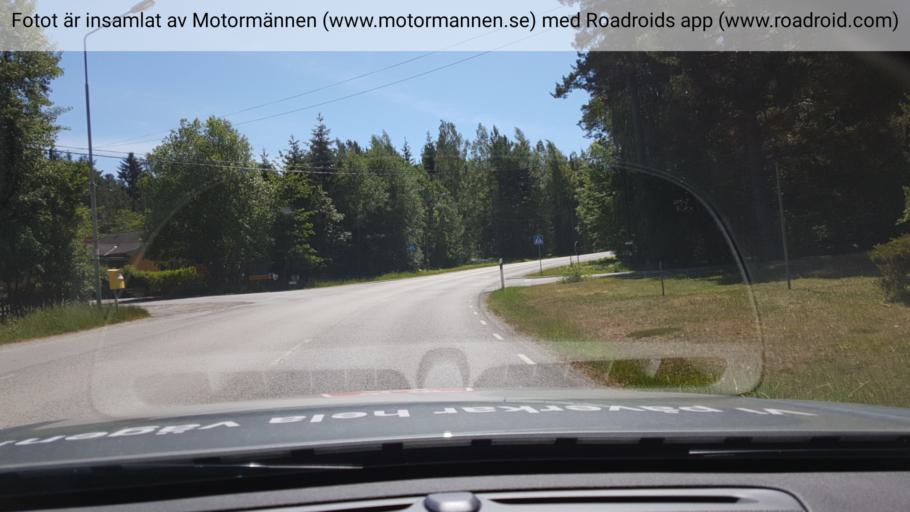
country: SE
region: Stockholm
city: Dalaro
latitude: 59.1442
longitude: 18.4156
